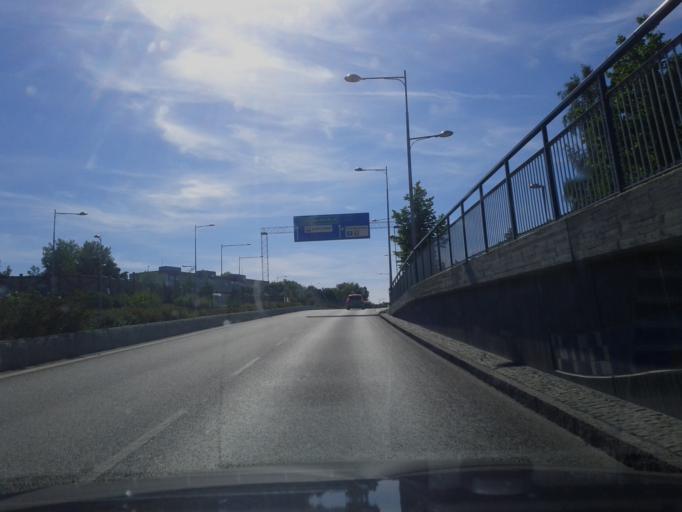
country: SE
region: Stockholm
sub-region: Taby Kommun
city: Taby
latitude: 59.4472
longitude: 18.0938
